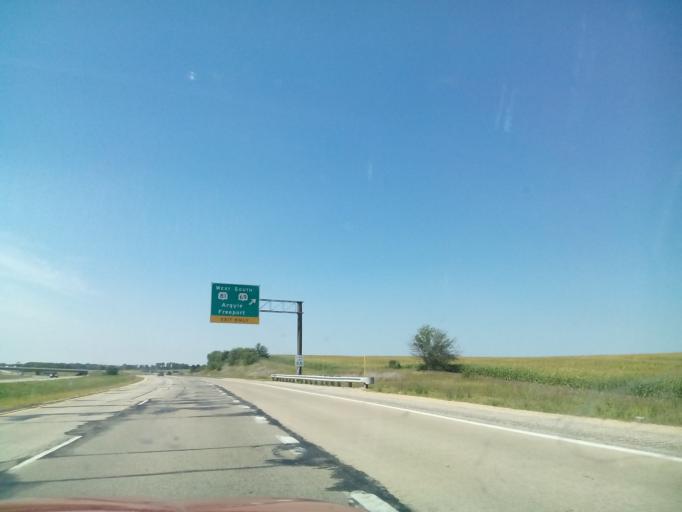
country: US
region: Wisconsin
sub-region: Green County
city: Monroe
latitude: 42.6170
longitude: -89.6462
